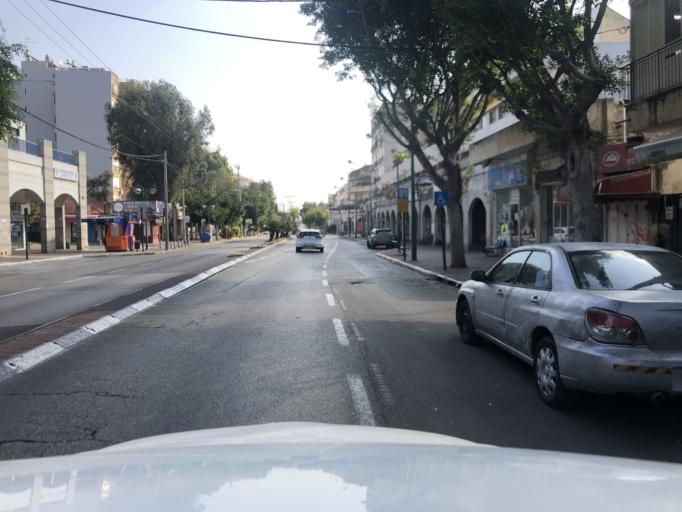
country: IL
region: Central District
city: Kfar Saba
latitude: 32.1750
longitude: 34.9098
